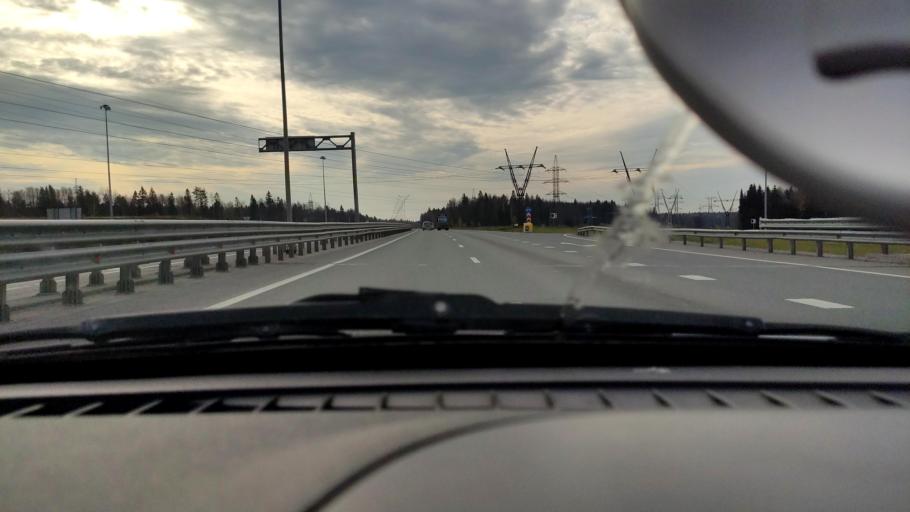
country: RU
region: Perm
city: Novyye Lyady
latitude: 58.0455
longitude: 56.4308
